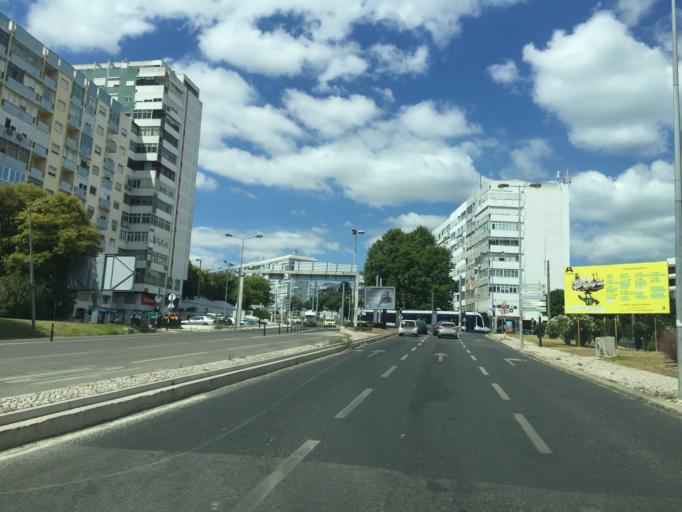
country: PT
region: Setubal
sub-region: Almada
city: Pragal
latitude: 38.6675
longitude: -9.1664
